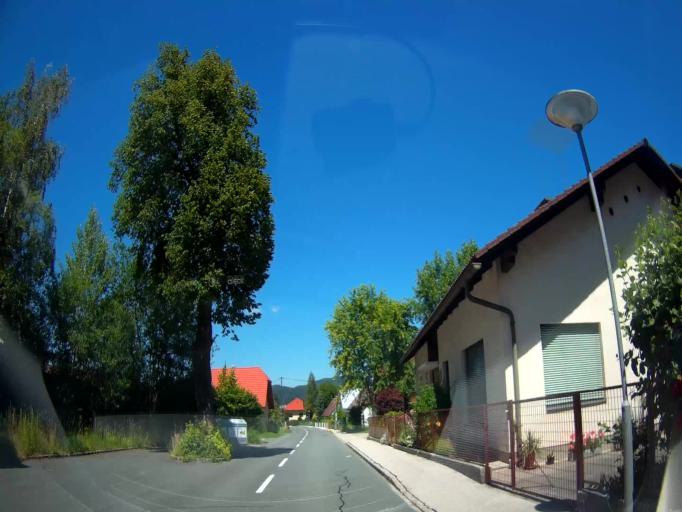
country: AT
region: Carinthia
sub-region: Politischer Bezirk Klagenfurt Land
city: Ferlach
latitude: 46.5186
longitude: 14.2971
